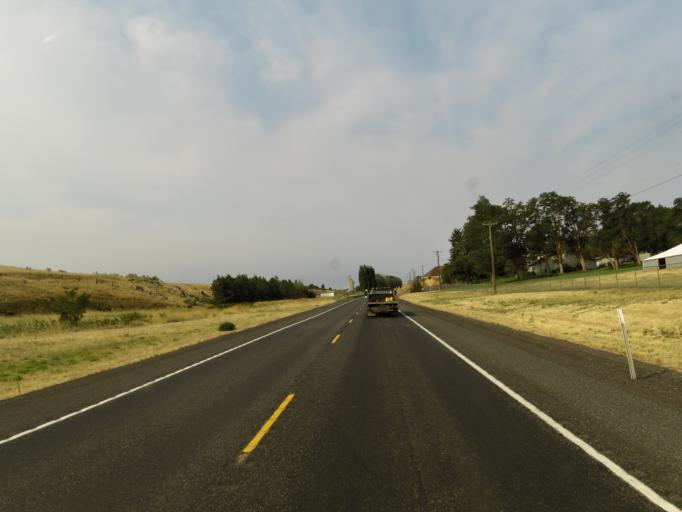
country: US
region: Oregon
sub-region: Sherman County
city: Moro
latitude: 45.4908
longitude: -120.7162
